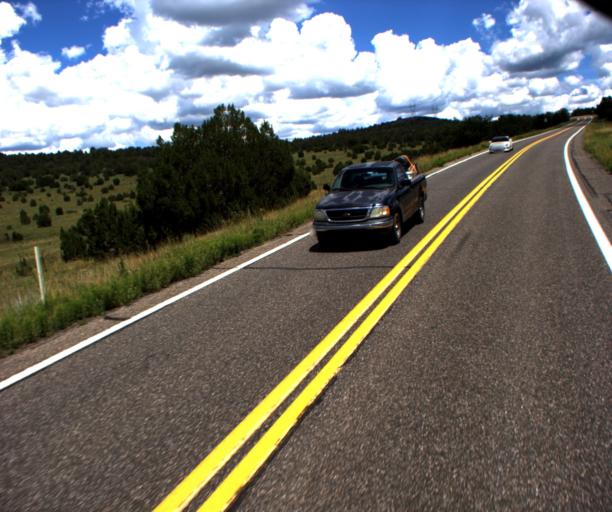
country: US
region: Arizona
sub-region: Gila County
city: Pine
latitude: 34.5090
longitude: -111.5581
